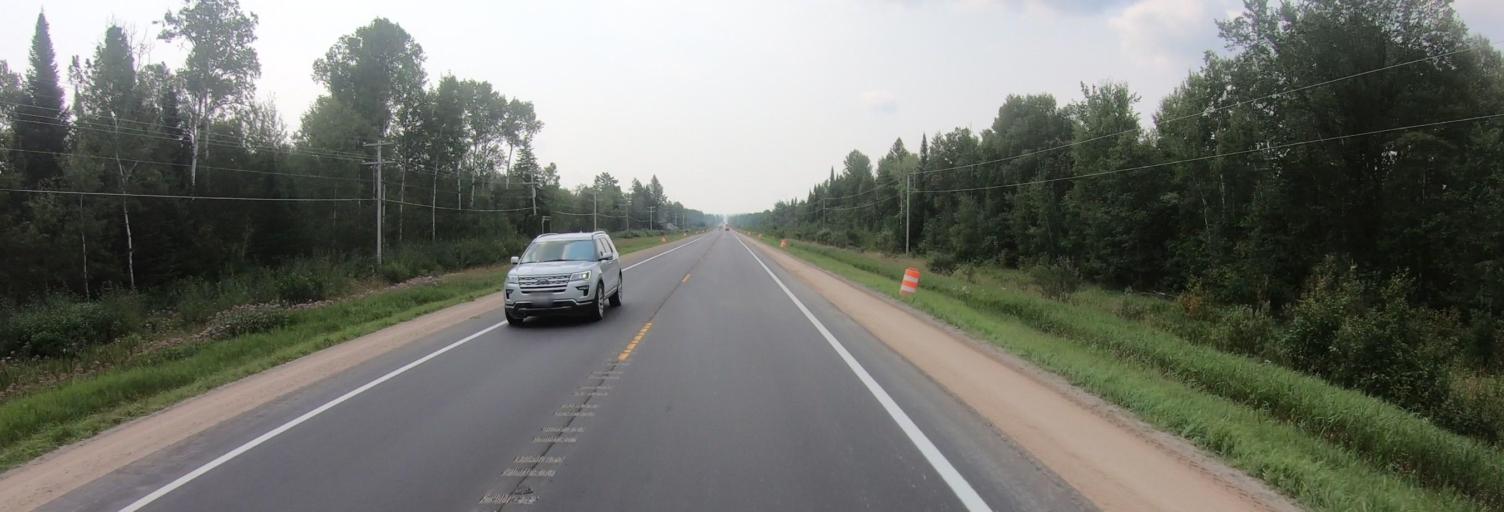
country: US
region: Michigan
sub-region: Luce County
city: Newberry
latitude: 46.3850
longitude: -85.5099
